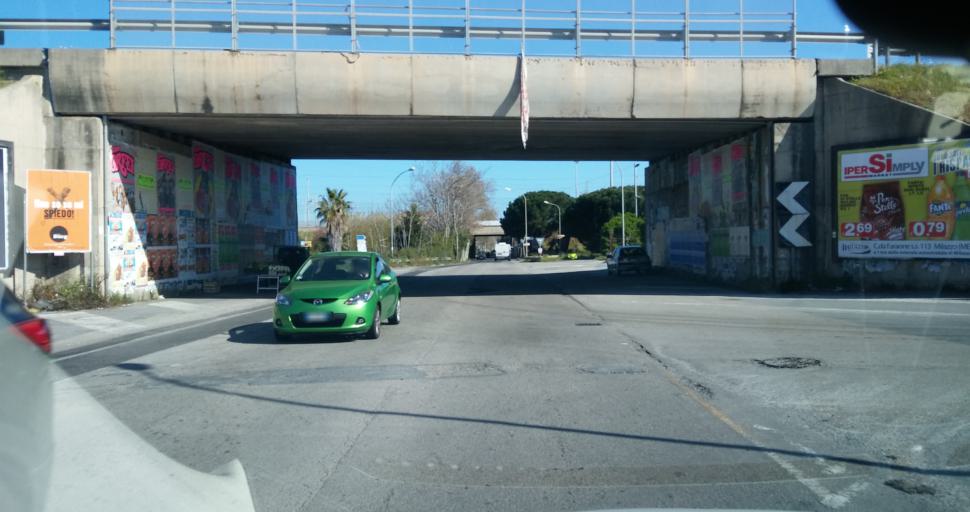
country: IT
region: Sicily
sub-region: Messina
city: Milazzo
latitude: 38.1969
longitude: 15.2523
